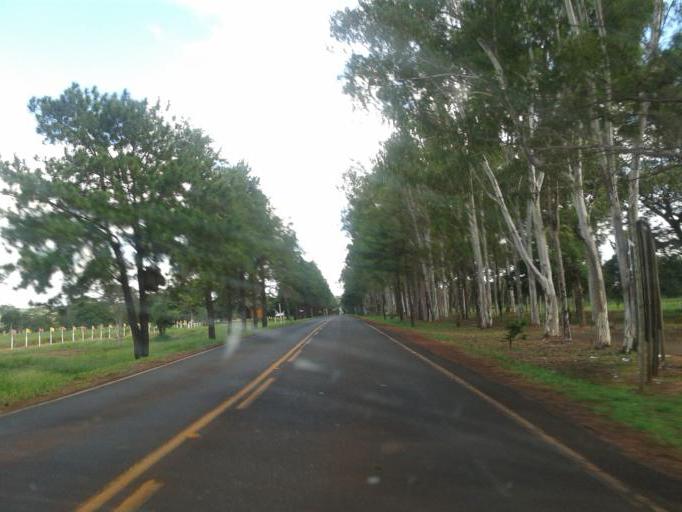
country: BR
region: Minas Gerais
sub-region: Santa Vitoria
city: Santa Vitoria
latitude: -18.8648
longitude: -50.1264
